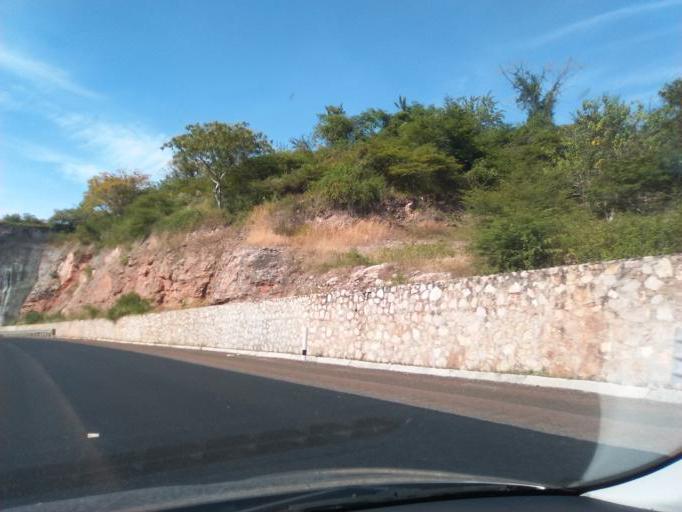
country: MX
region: Guerrero
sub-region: Huitzuco de los Figueroa
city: Ciudad de Huitzuco
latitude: 18.2016
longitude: -99.2069
